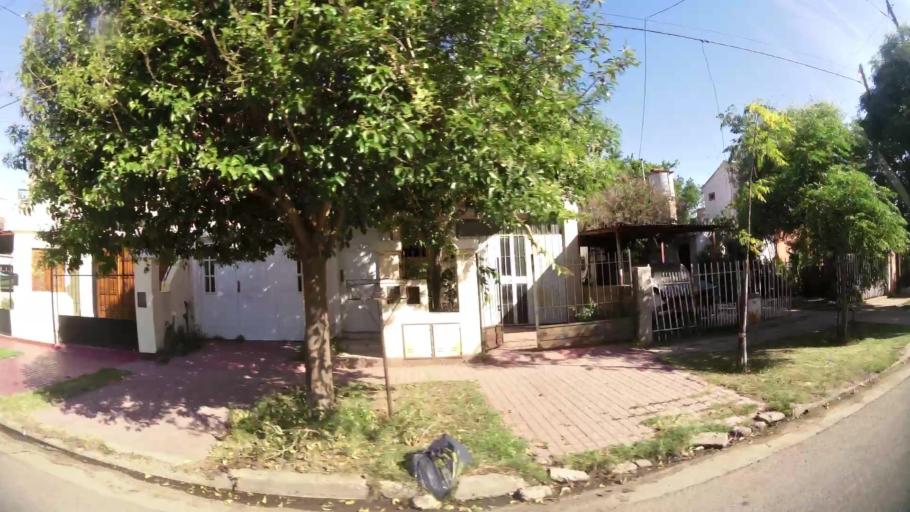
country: AR
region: Cordoba
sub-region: Departamento de Capital
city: Cordoba
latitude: -31.3635
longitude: -64.1891
